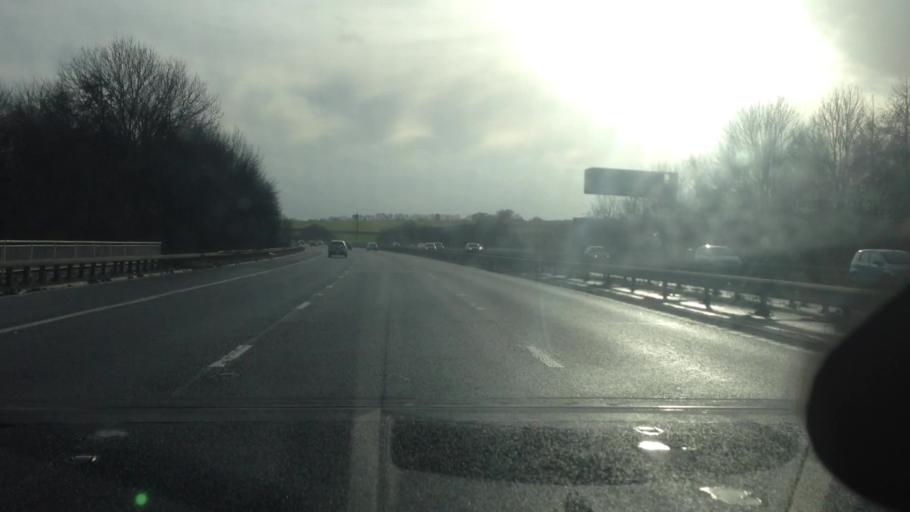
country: GB
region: England
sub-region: Barnsley
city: Darton
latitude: 53.6038
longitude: -1.5512
